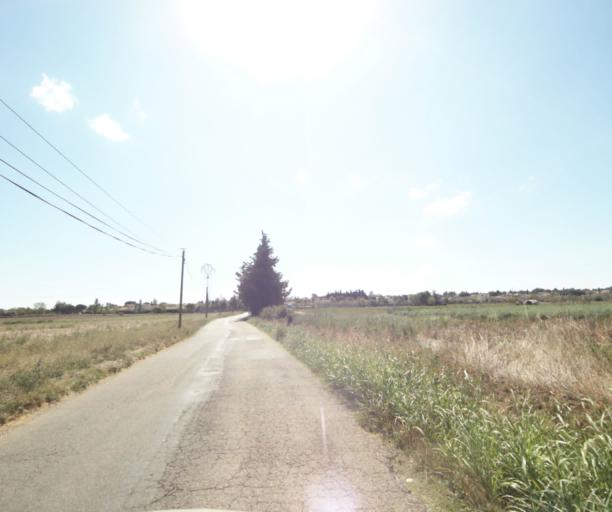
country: FR
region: Languedoc-Roussillon
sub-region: Departement du Gard
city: Bouillargues
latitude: 43.8072
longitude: 4.4212
